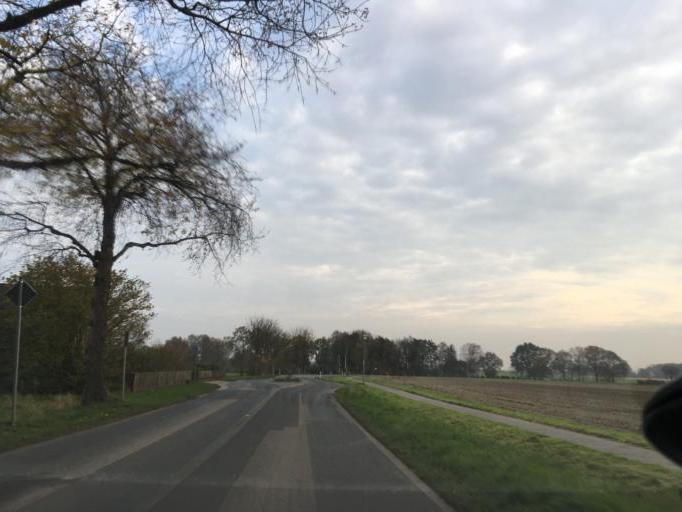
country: DE
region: Lower Saxony
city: Bergen
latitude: 52.8385
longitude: 9.9764
